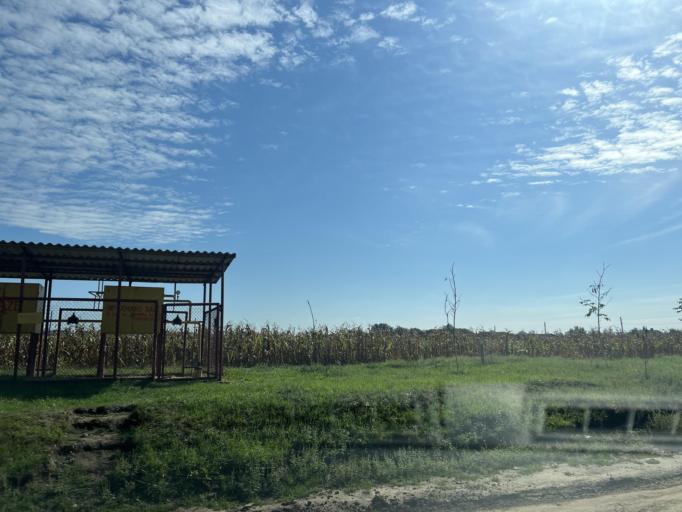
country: MD
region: Ungheni
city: Ungheni
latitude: 47.2000
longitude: 27.8177
